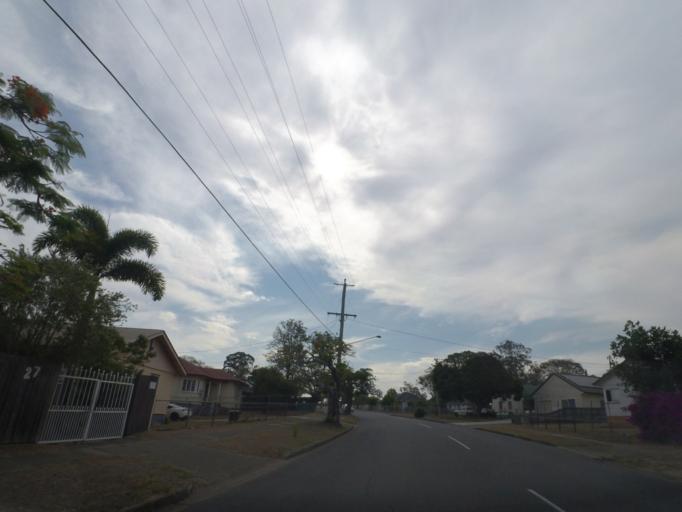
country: AU
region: Queensland
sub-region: Brisbane
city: Richlands
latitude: -27.5914
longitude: 152.9632
